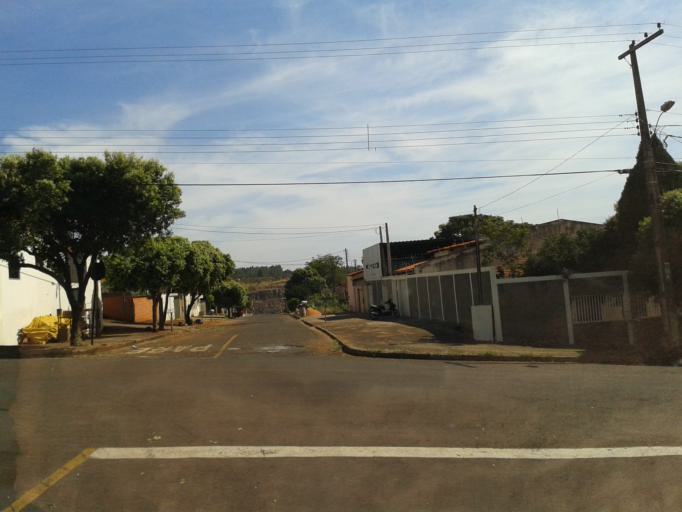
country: BR
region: Minas Gerais
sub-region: Ituiutaba
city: Ituiutaba
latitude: -18.9617
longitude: -49.4668
